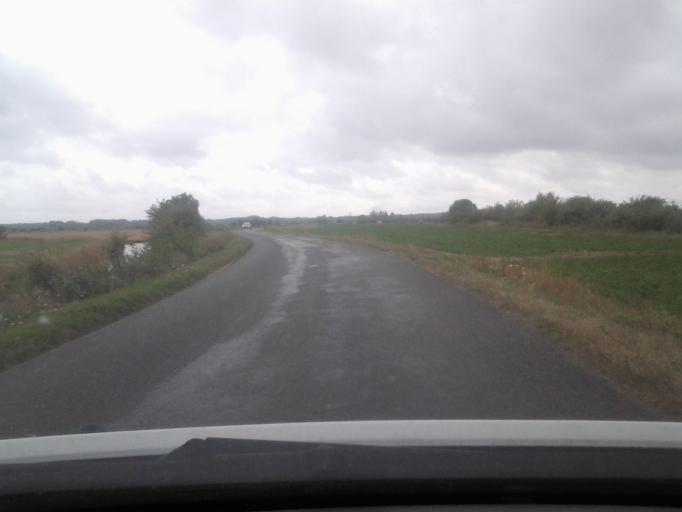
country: FR
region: Pays de la Loire
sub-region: Departement de la Vendee
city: Angles
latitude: 46.3905
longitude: -1.4305
